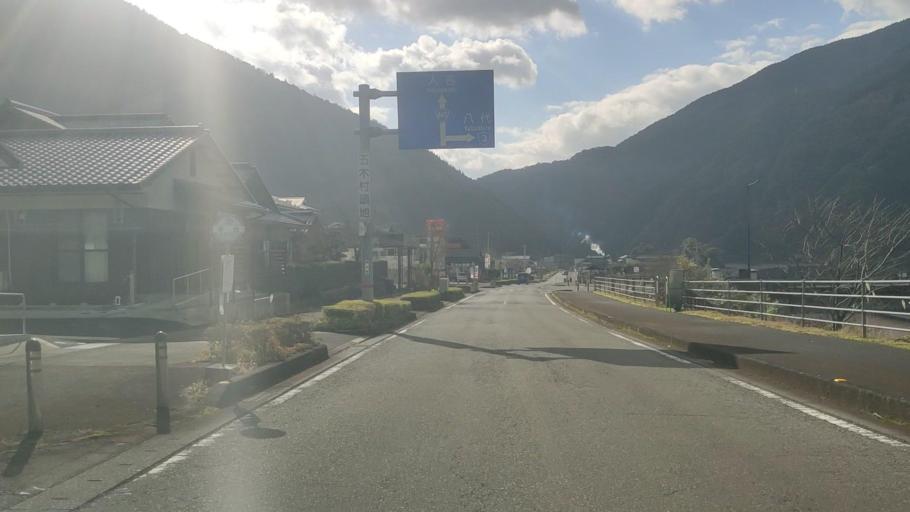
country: JP
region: Kumamoto
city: Hitoyoshi
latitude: 32.4008
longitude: 130.8264
